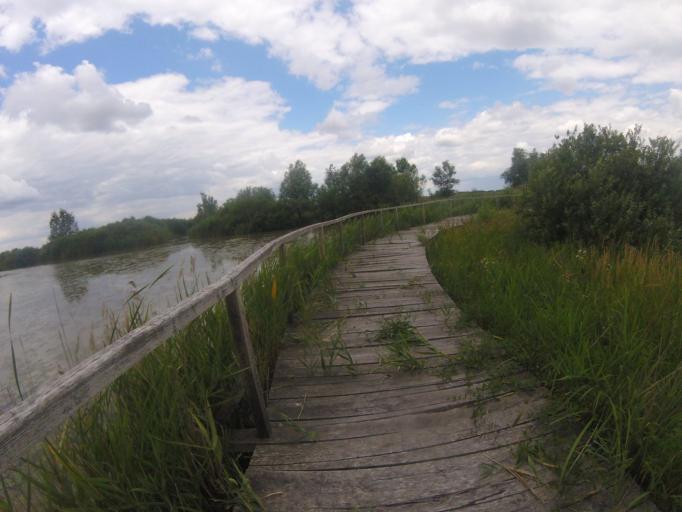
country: HU
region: Hajdu-Bihar
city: Egyek
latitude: 47.5688
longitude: 20.9377
